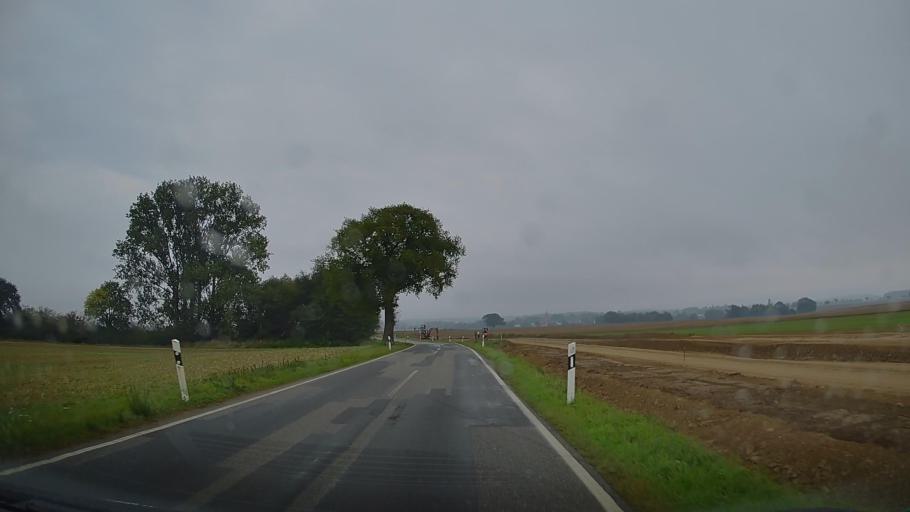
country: DE
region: Mecklenburg-Vorpommern
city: Kalkhorst
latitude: 53.9775
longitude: 11.0249
